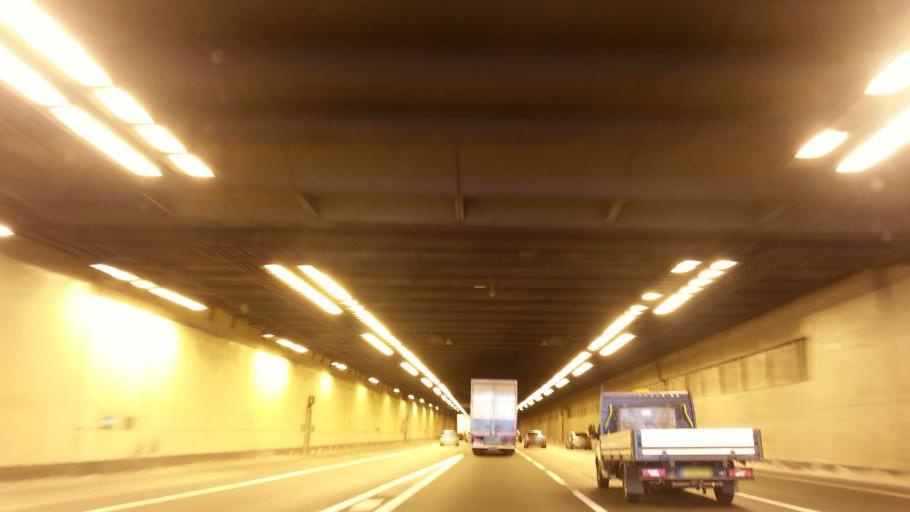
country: GB
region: England
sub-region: Hertfordshire
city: Waltham Cross
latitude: 51.6829
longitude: -0.0429
